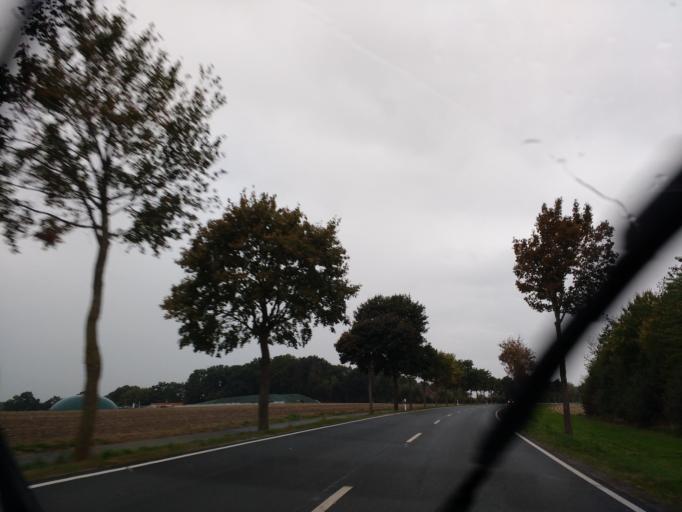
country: DE
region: North Rhine-Westphalia
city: Rietberg
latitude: 51.7489
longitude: 8.4596
